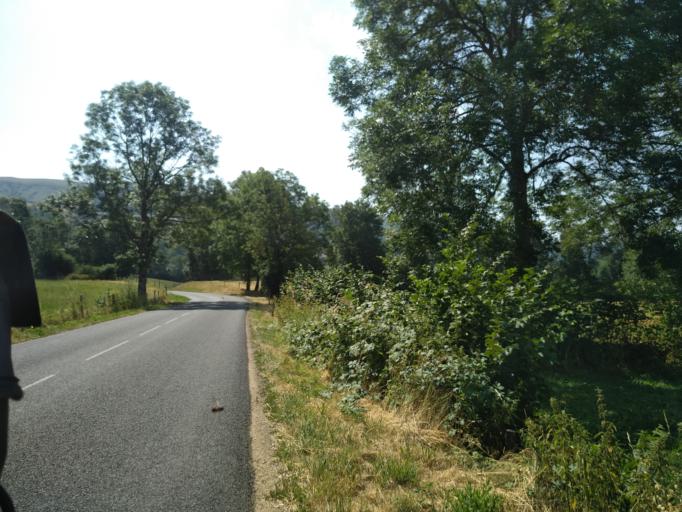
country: FR
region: Auvergne
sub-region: Departement du Cantal
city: Riom-es-Montagnes
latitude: 45.1871
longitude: 2.7157
